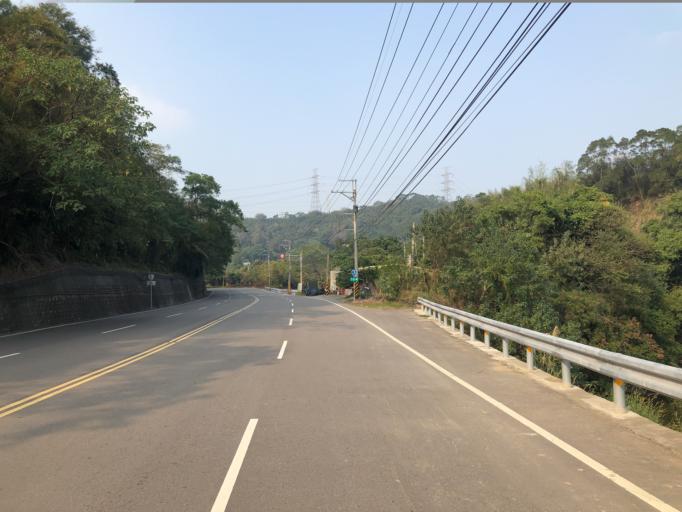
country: TW
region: Taiwan
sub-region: Miaoli
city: Miaoli
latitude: 24.6120
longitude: 120.9584
